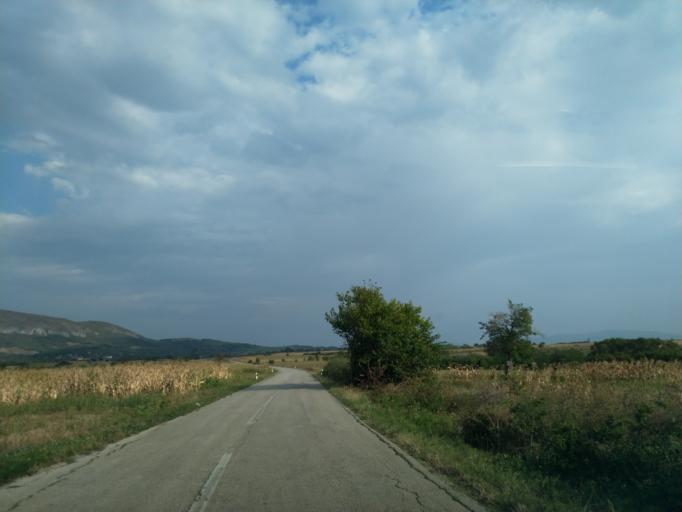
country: RS
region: Central Serbia
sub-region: Pomoravski Okrug
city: Paracin
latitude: 43.8267
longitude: 21.5199
